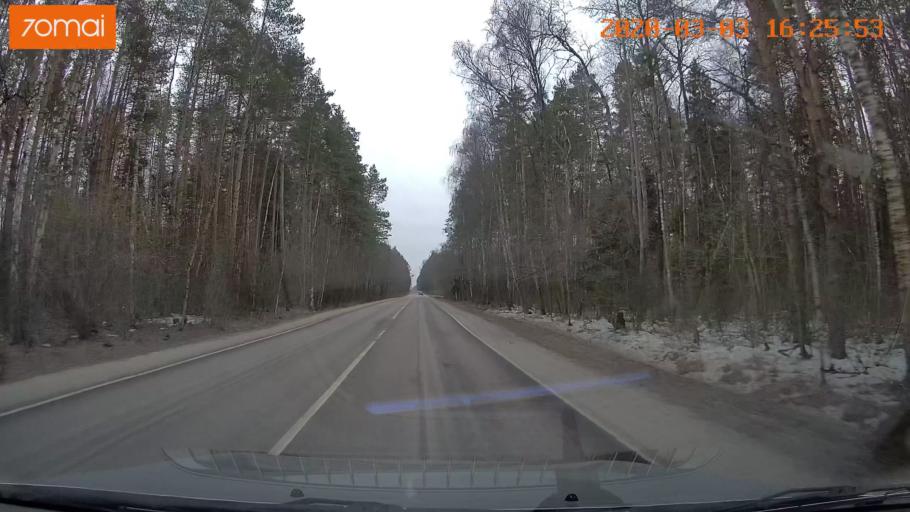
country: RU
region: Moskovskaya
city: Konobeyevo
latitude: 55.4464
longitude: 38.6597
